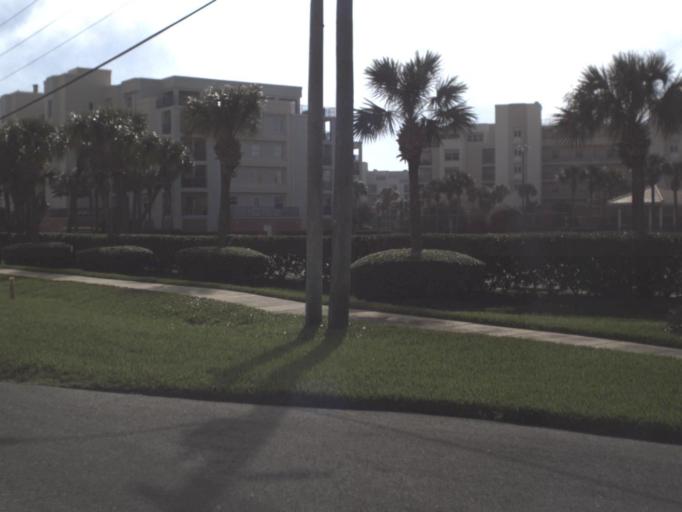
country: US
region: Florida
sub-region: Volusia County
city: Edgewater
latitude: 28.9755
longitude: -80.8574
